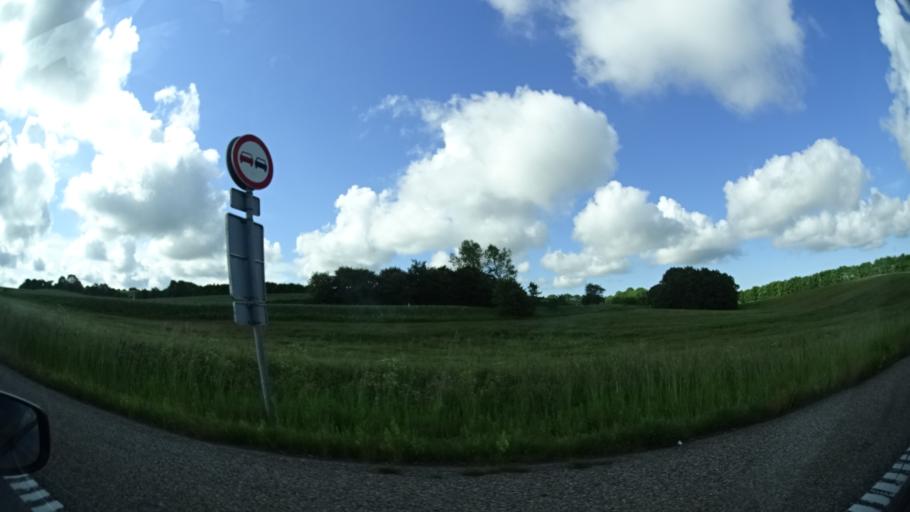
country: DK
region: Central Jutland
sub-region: Syddjurs Kommune
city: Ronde
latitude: 56.2959
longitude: 10.5644
